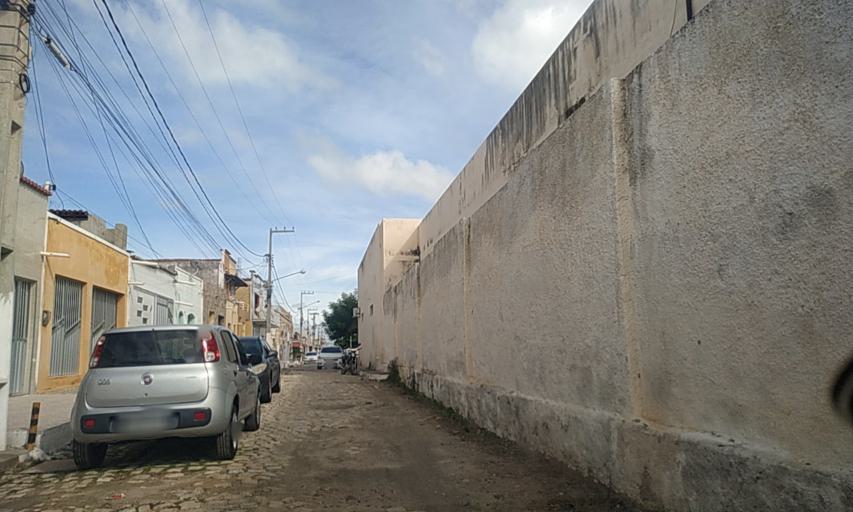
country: BR
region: Rio Grande do Norte
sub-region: Areia Branca
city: Areia Branca
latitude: -4.9582
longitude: -37.1318
